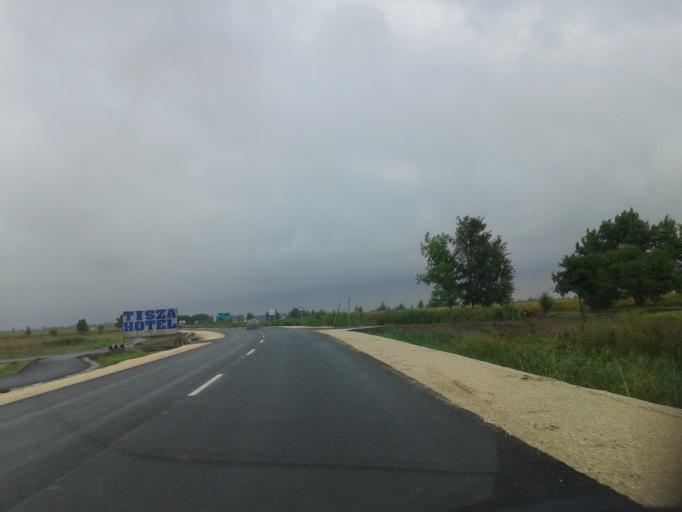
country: HU
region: Csongrad
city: Domaszek
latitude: 46.2517
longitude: 20.0777
